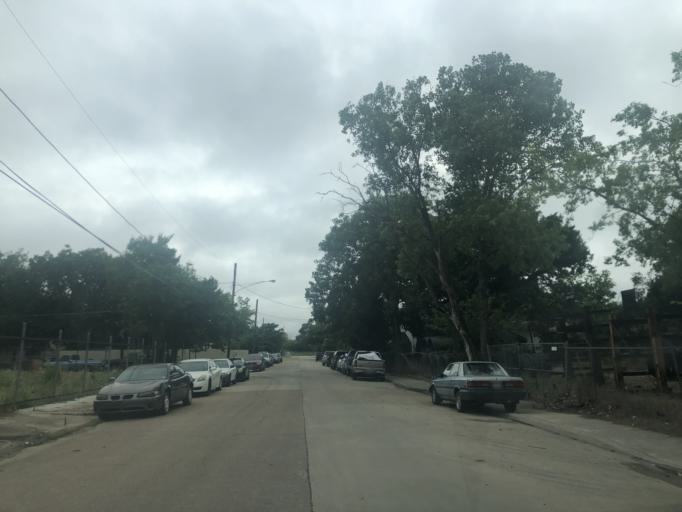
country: US
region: Texas
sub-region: Dallas County
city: Cockrell Hill
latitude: 32.7769
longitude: -96.8578
